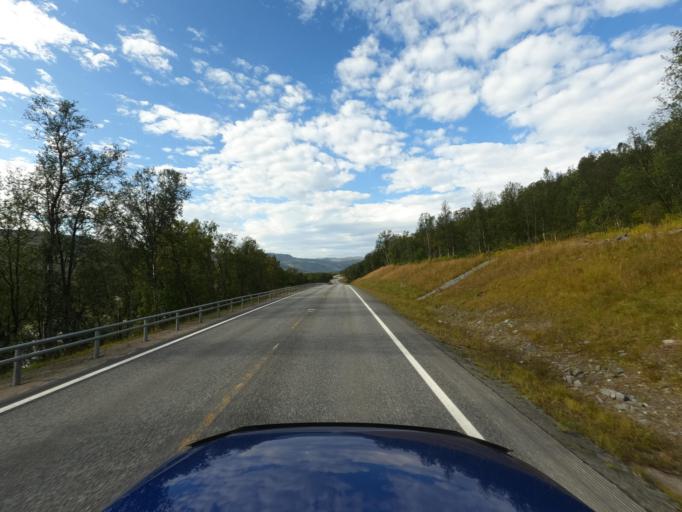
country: NO
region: Finnmark Fylke
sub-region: Kvalsund
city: Kvalsund
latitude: 70.4431
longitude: 24.4553
